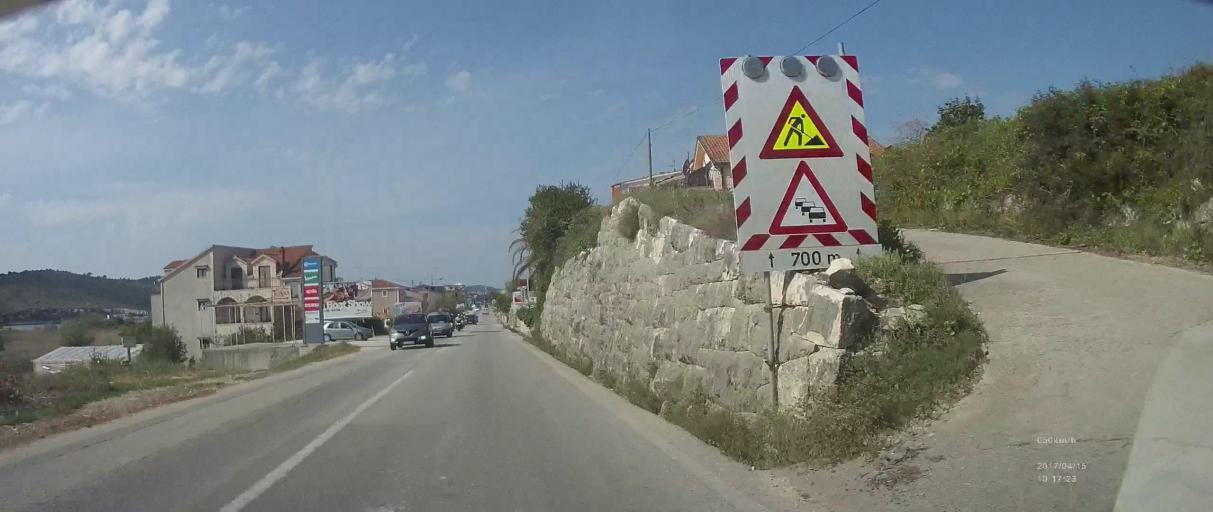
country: HR
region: Splitsko-Dalmatinska
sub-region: Grad Trogir
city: Trogir
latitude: 43.5266
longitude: 16.2709
